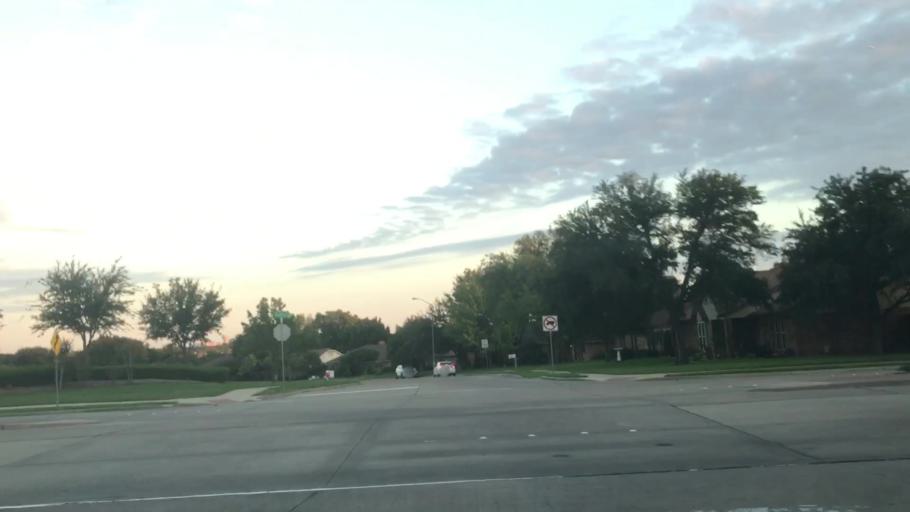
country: US
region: Texas
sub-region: Dallas County
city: Carrollton
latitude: 32.9747
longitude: -96.8763
